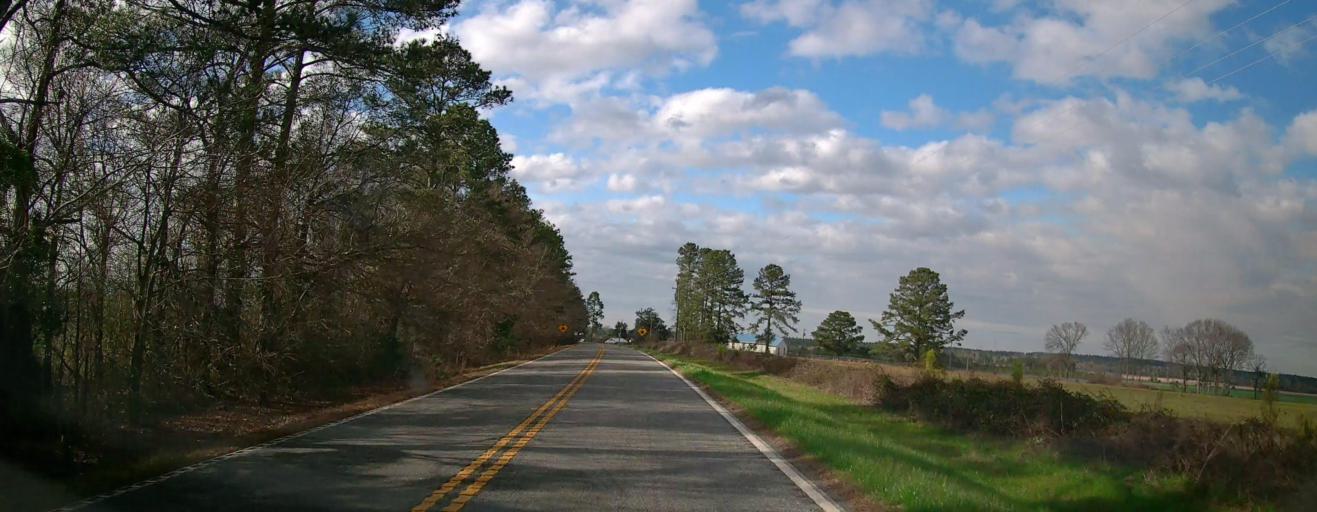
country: US
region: Georgia
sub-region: Marion County
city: Buena Vista
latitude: 32.4508
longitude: -84.4428
